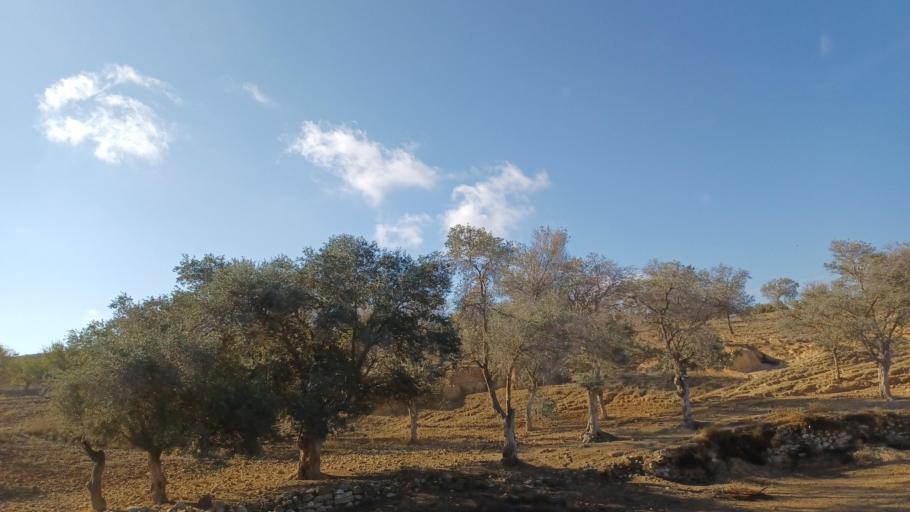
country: CY
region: Pafos
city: Polis
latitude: 34.9996
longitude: 32.3766
